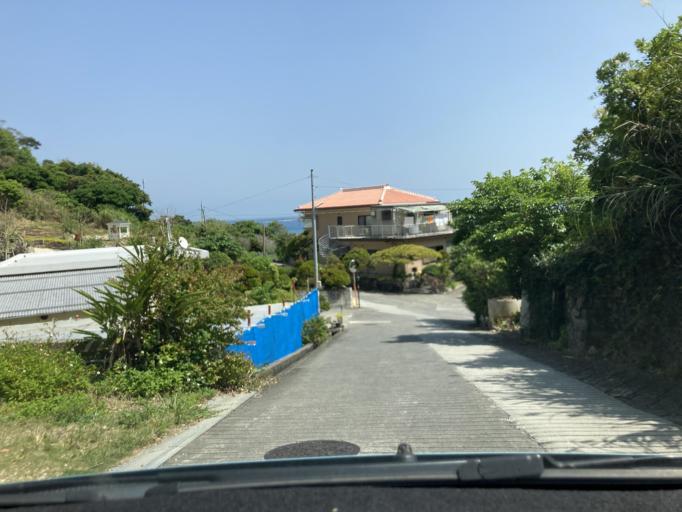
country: JP
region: Okinawa
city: Ginowan
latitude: 26.1624
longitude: 127.8144
